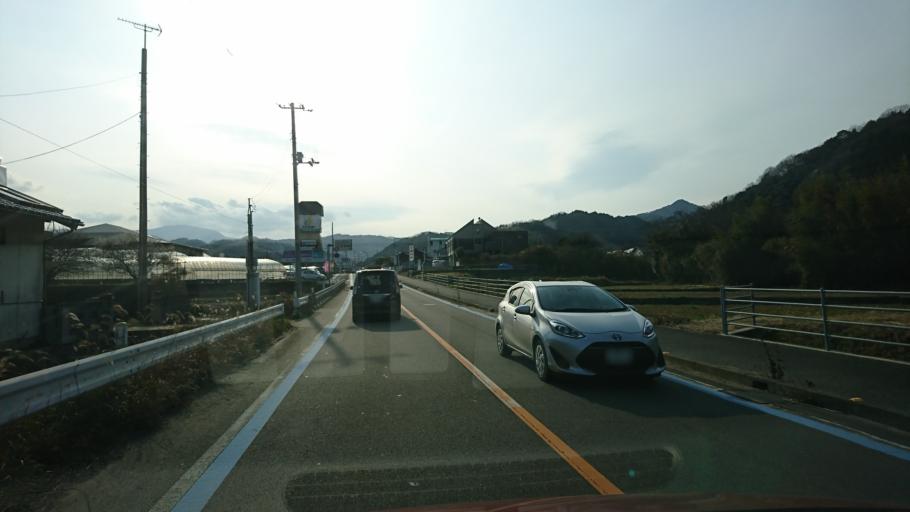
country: JP
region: Ehime
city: Hojo
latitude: 34.0234
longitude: 132.9448
